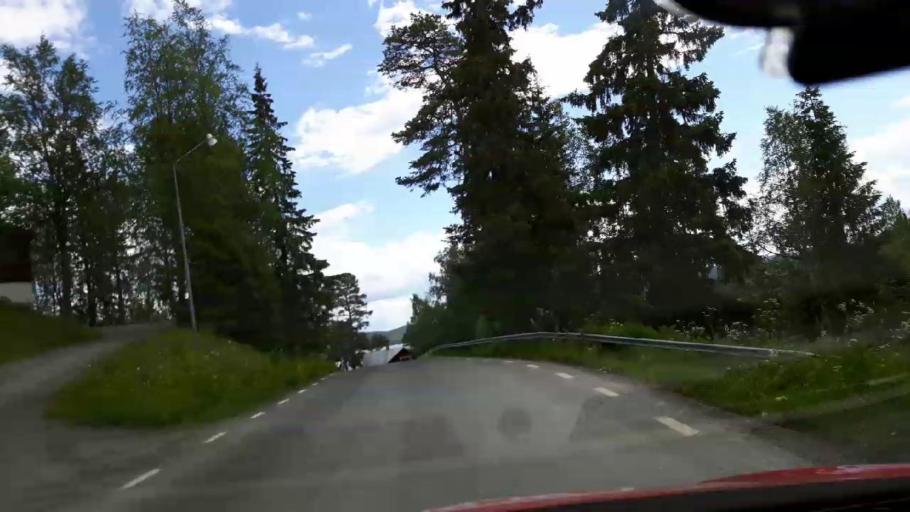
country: SE
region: Jaemtland
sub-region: Krokoms Kommun
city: Valla
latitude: 64.0702
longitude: 14.1362
